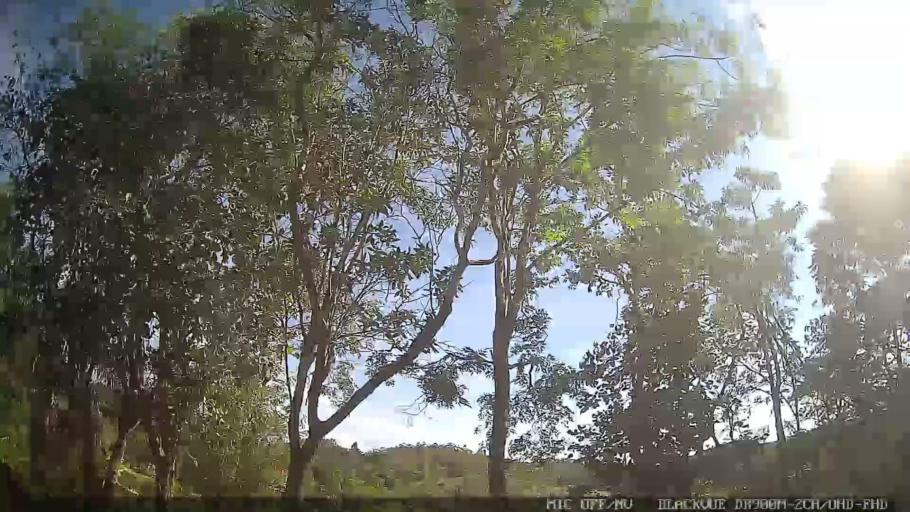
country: BR
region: Sao Paulo
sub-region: Serra Negra
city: Serra Negra
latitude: -22.6056
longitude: -46.7245
